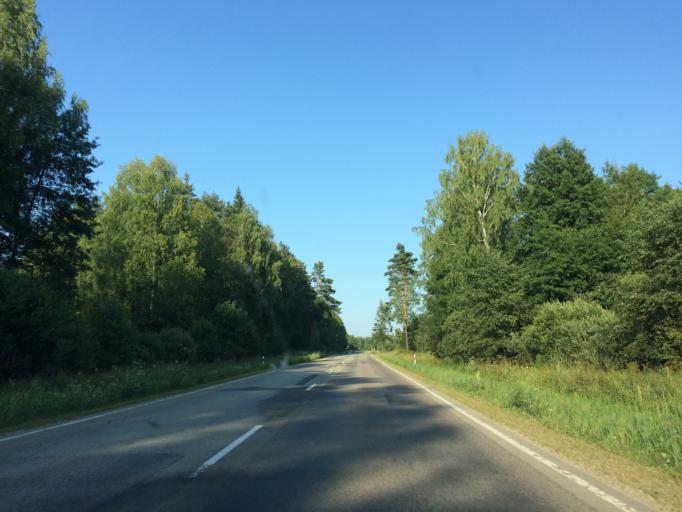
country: LV
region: Ludzas Rajons
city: Ludza
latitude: 56.5357
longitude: 27.5606
